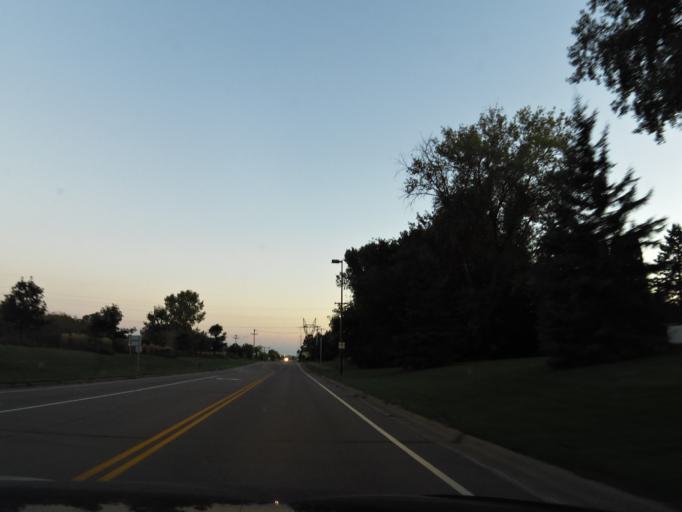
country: US
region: Minnesota
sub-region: Washington County
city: Oakdale
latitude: 44.9551
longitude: -92.9646
